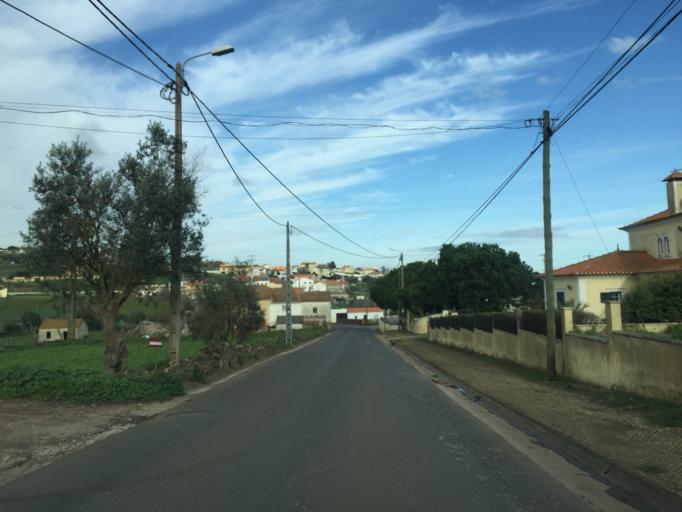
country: PT
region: Lisbon
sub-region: Sintra
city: Almargem
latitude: 38.8330
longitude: -9.2510
